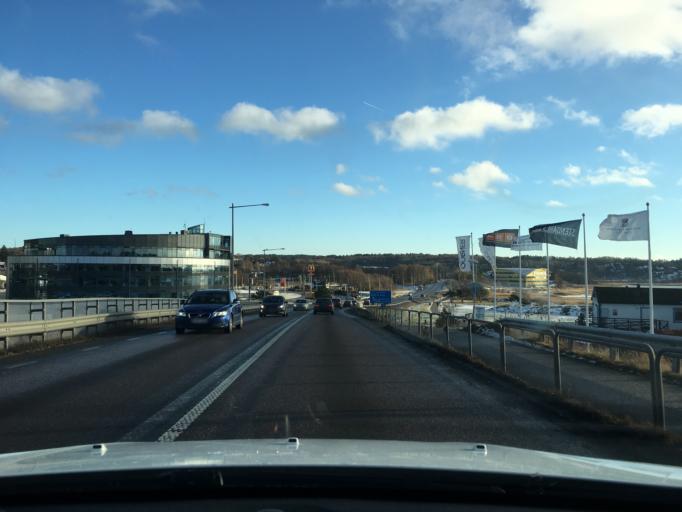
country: SE
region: Vaestra Goetaland
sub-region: Stenungsunds Kommun
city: Stenungsund
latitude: 58.0635
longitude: 11.8124
